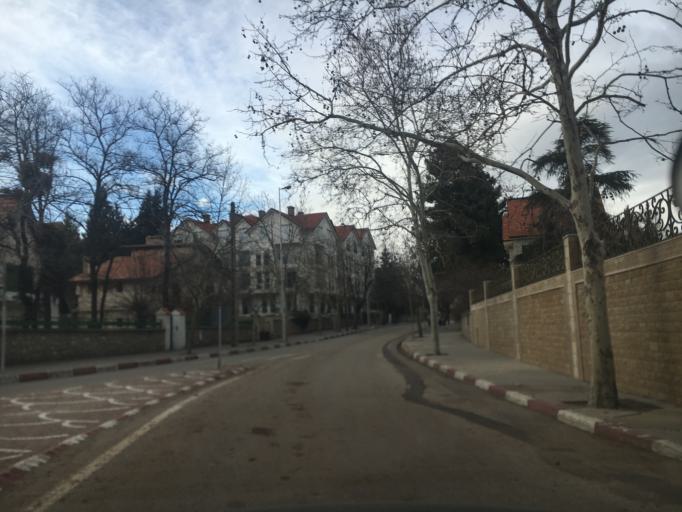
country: MA
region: Meknes-Tafilalet
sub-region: Ifrane
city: Ifrane
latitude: 33.5270
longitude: -5.1121
